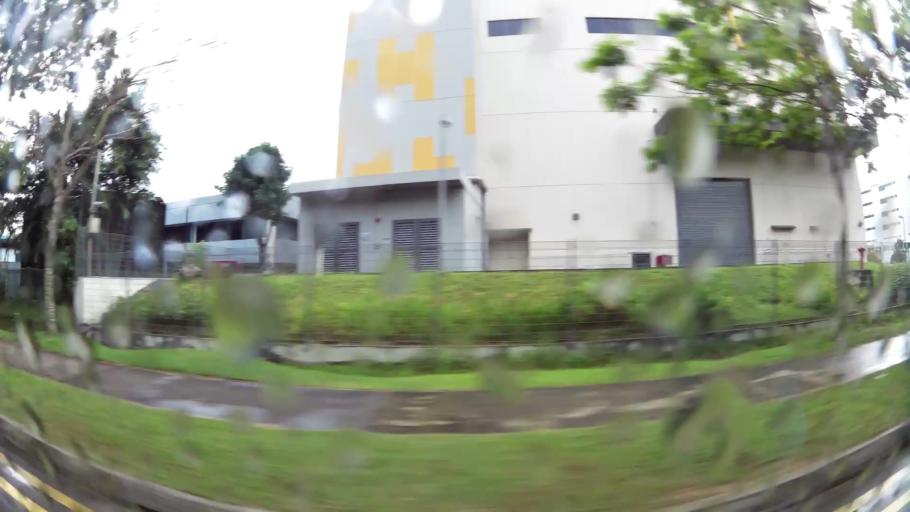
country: MY
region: Johor
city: Kampung Pasir Gudang Baru
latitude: 1.3916
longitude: 103.8475
